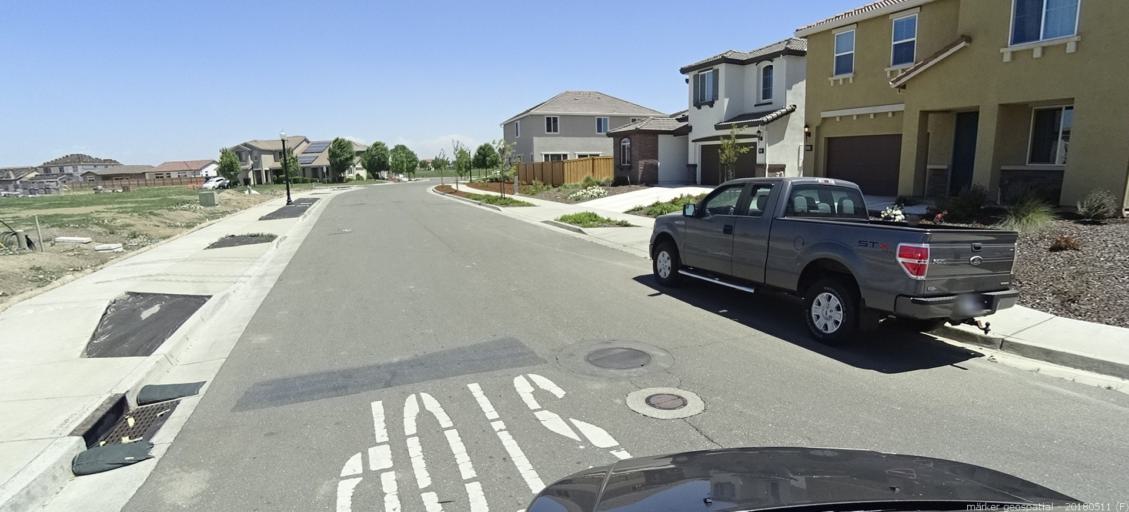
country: US
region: California
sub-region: Yolo County
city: West Sacramento
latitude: 38.6463
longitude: -121.5520
